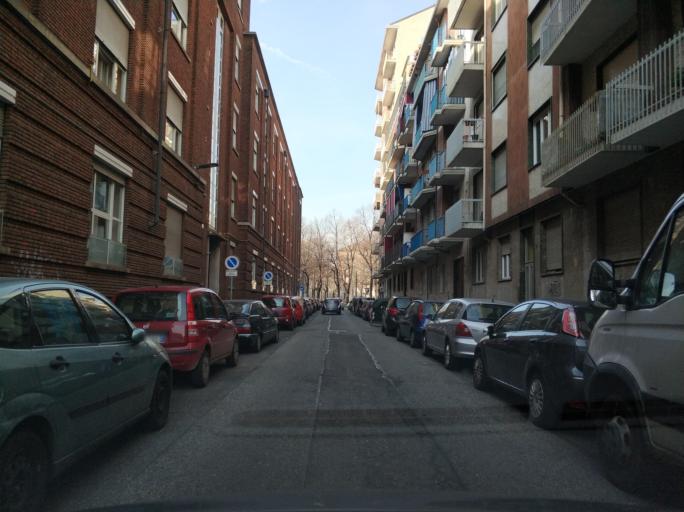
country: IT
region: Piedmont
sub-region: Provincia di Torino
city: Turin
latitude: 45.0821
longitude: 7.6797
